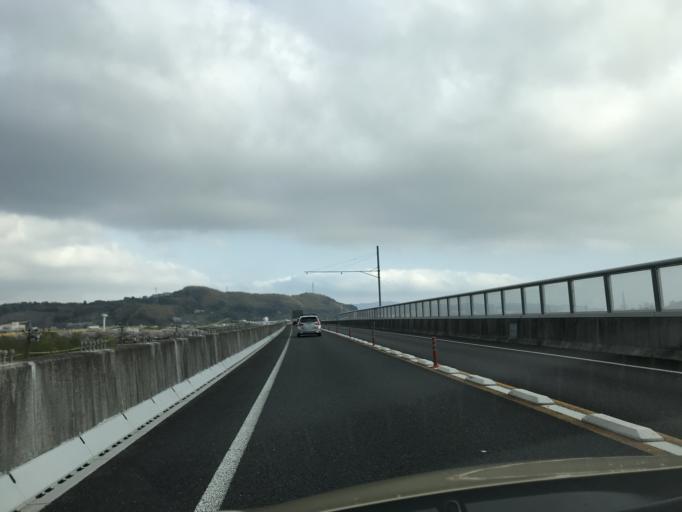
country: JP
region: Shizuoka
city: Shizuoka-shi
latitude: 35.0190
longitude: 138.3908
